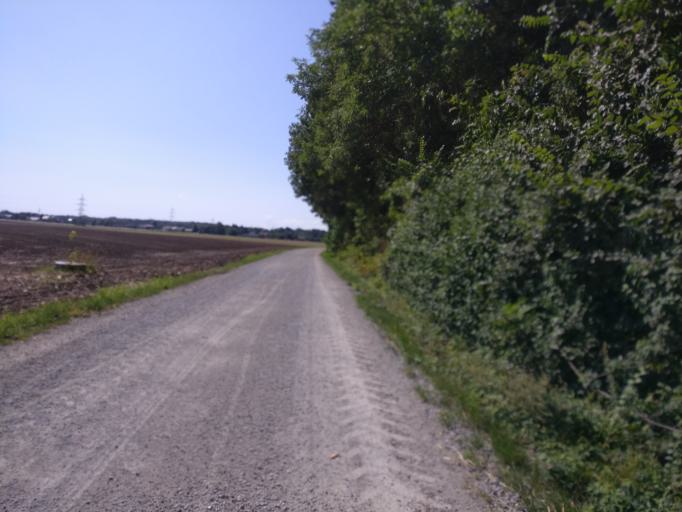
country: AT
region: Lower Austria
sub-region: Politischer Bezirk Wiener Neustadt
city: Ebenfurth
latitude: 47.8805
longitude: 16.3437
